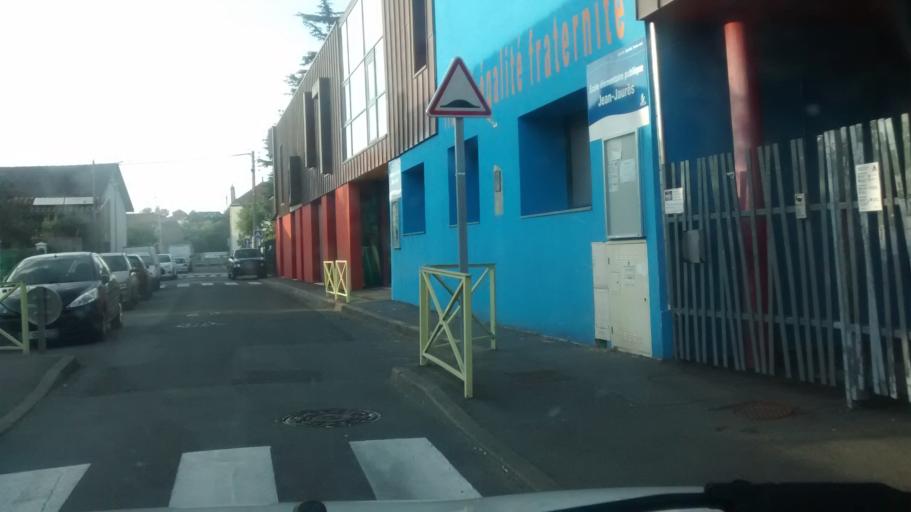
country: FR
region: Pays de la Loire
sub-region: Departement de la Loire-Atlantique
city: Reze
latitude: 47.1941
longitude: -1.5795
